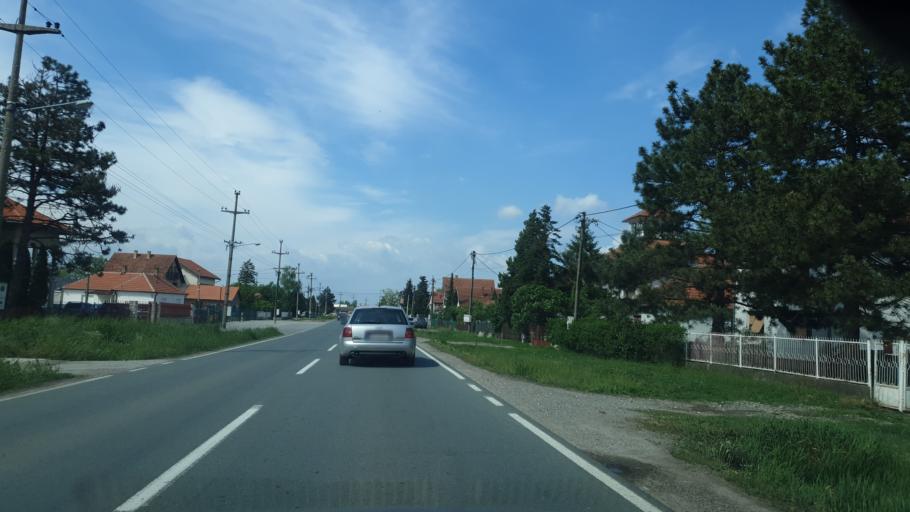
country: RS
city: Zvecka
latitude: 44.6396
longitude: 20.1833
